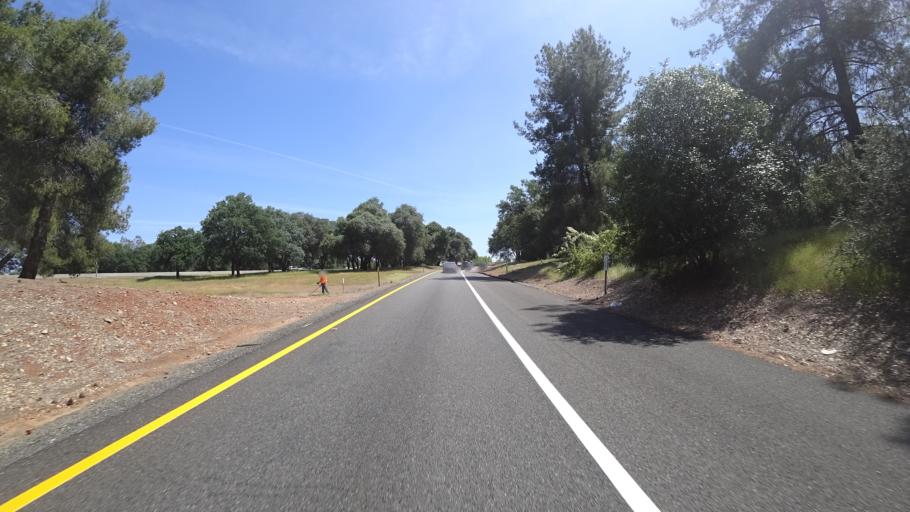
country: US
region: California
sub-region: Shasta County
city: Redding
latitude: 40.5837
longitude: -122.3620
